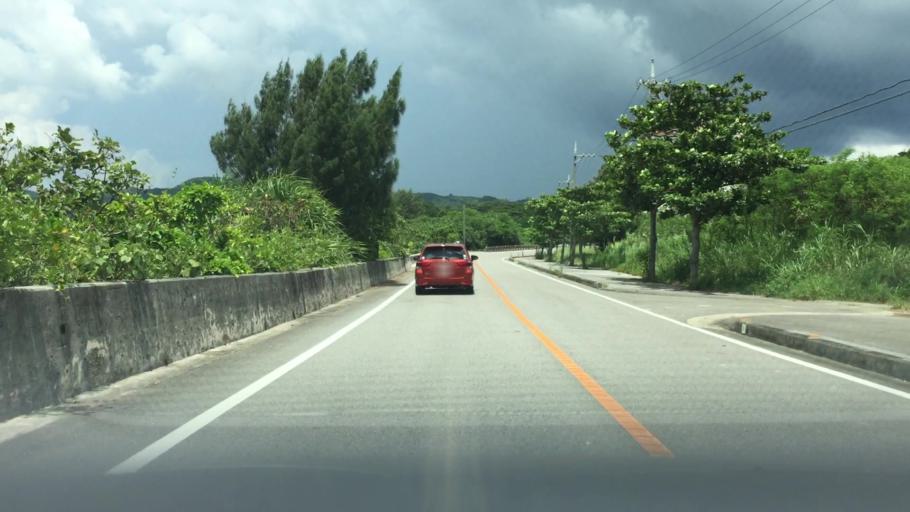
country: JP
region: Okinawa
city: Ishigaki
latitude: 24.4343
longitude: 124.1214
